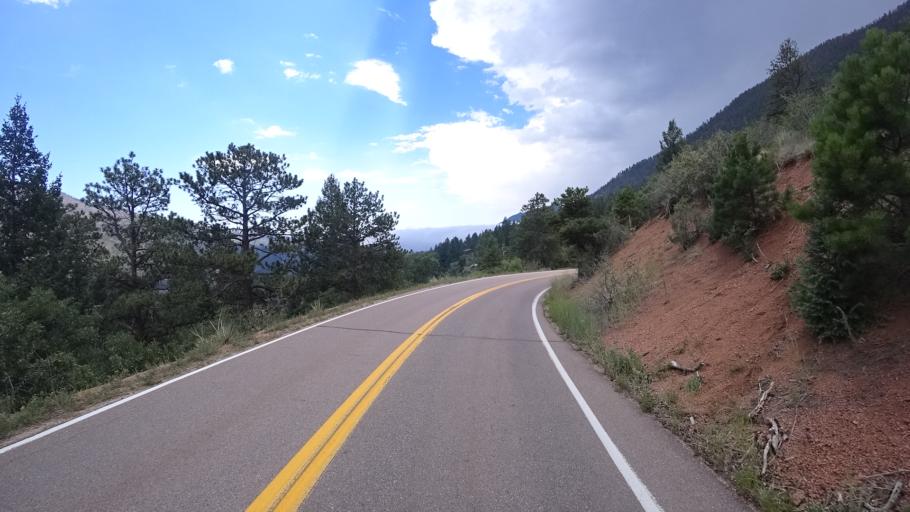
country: US
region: Colorado
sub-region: El Paso County
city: Cascade-Chipita Park
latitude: 38.9097
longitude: -104.9826
